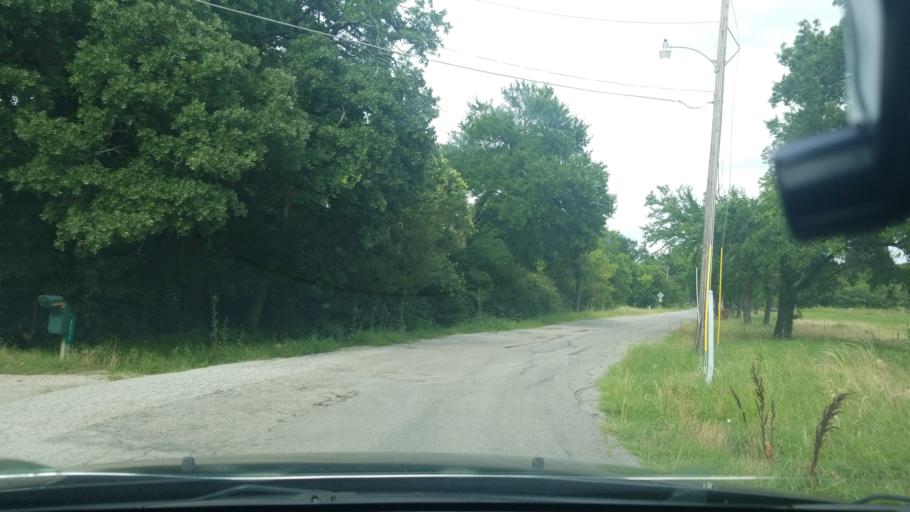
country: US
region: Texas
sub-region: Dallas County
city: Balch Springs
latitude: 32.7553
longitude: -96.6370
